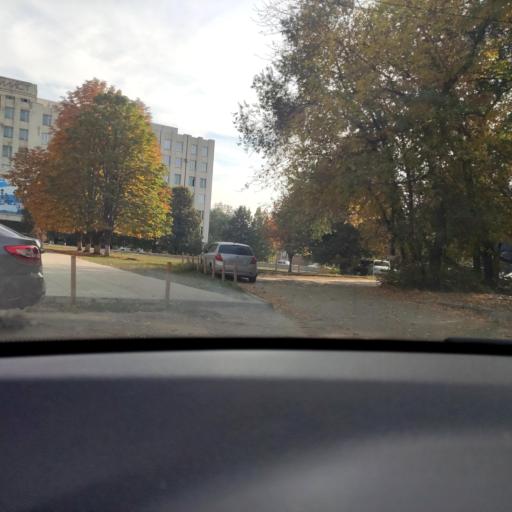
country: RU
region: Samara
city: Samara
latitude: 53.1964
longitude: 50.2220
